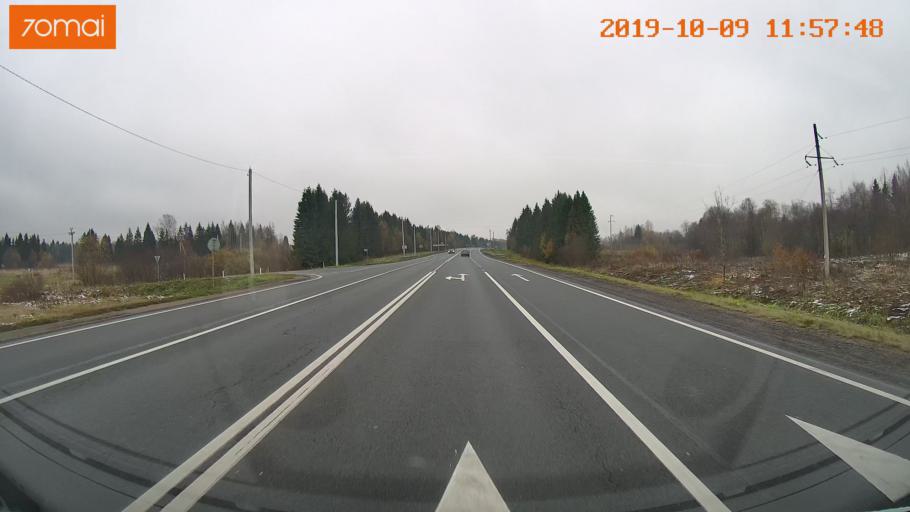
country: RU
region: Vologda
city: Gryazovets
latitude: 58.7272
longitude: 40.2947
